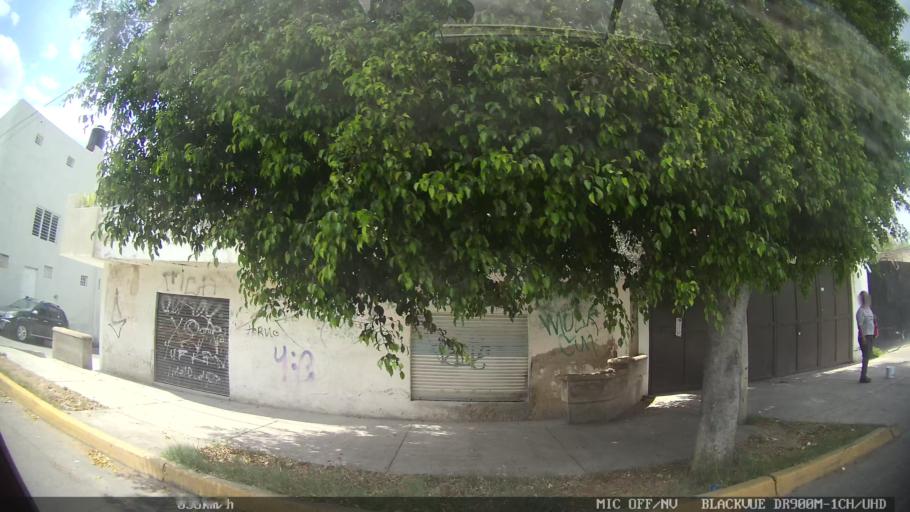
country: MX
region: Jalisco
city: Tlaquepaque
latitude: 20.6490
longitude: -103.2818
